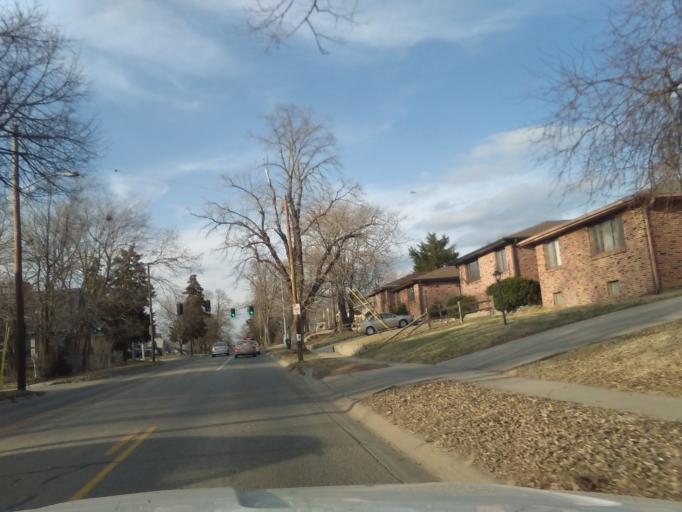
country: US
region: Nebraska
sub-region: Lancaster County
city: Lincoln
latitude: 40.7837
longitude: -96.7028
